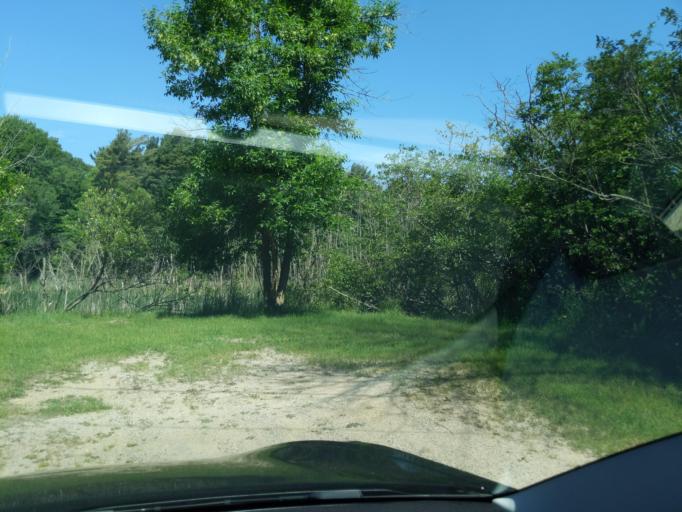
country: US
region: Michigan
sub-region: Muskegon County
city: Montague
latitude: 43.3871
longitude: -86.4235
